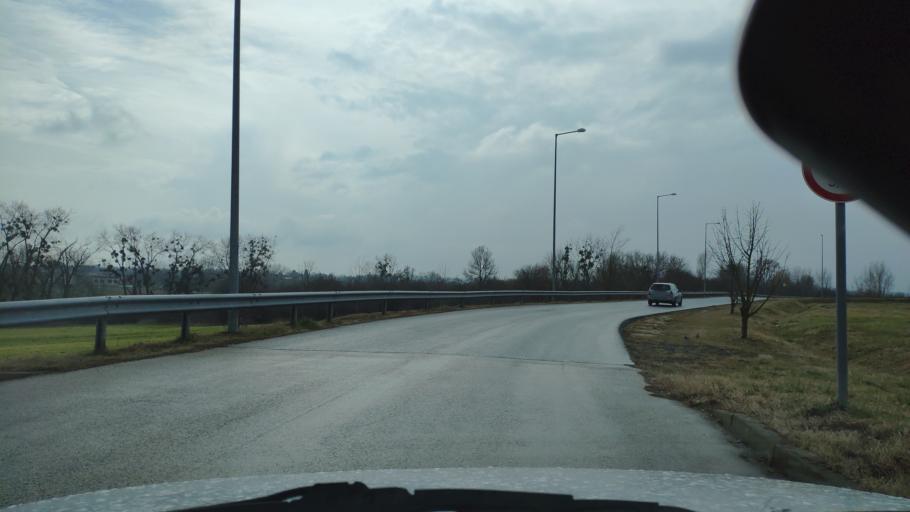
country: HU
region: Zala
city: Nagykanizsa
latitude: 46.4571
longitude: 17.0176
